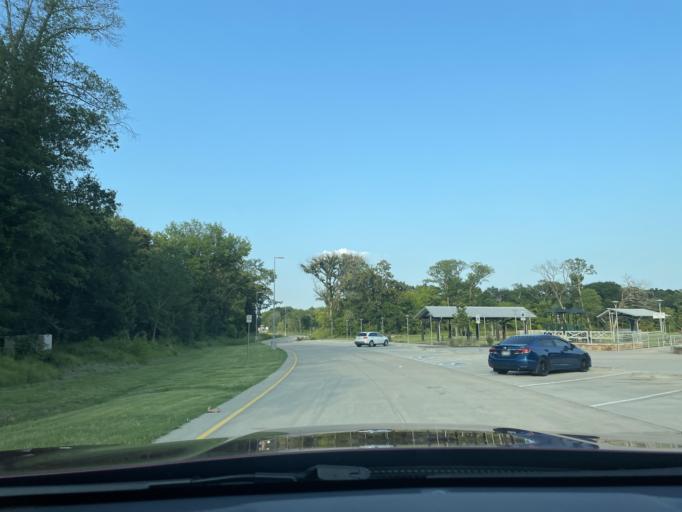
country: US
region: Texas
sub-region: Hunt County
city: Commerce
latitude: 33.1304
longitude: -95.8158
